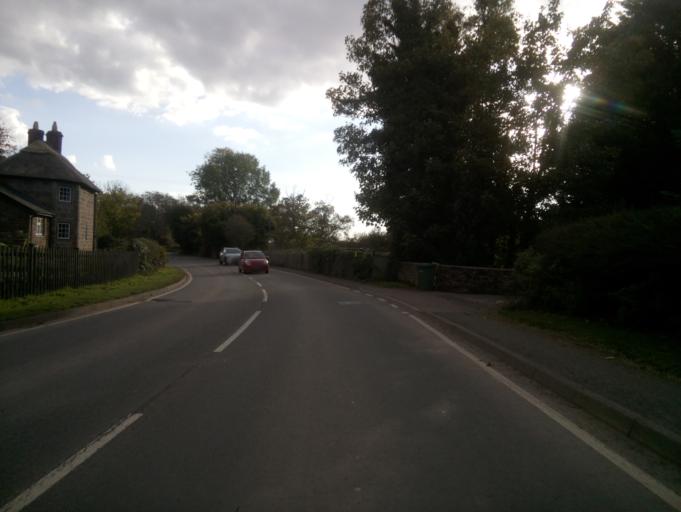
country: GB
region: England
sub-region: Herefordshire
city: Sutton
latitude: 52.0640
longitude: -2.6633
